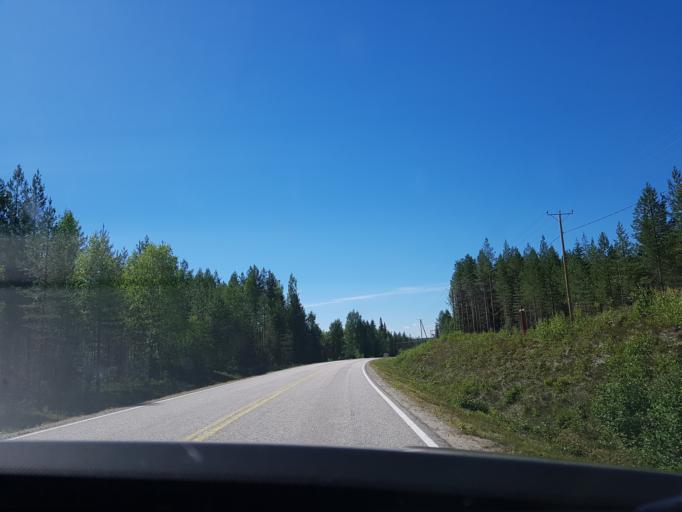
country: FI
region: Kainuu
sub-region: Kehys-Kainuu
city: Kuhmo
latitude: 64.1708
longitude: 29.6577
